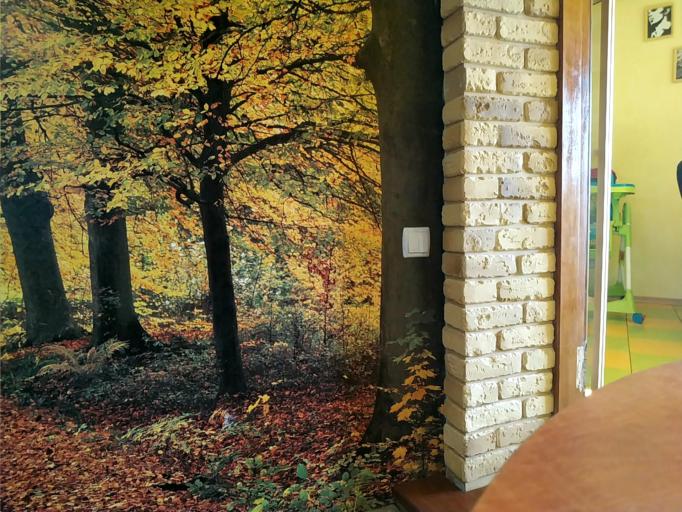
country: RU
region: Vologda
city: Nelazskoye
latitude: 59.4108
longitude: 37.6086
